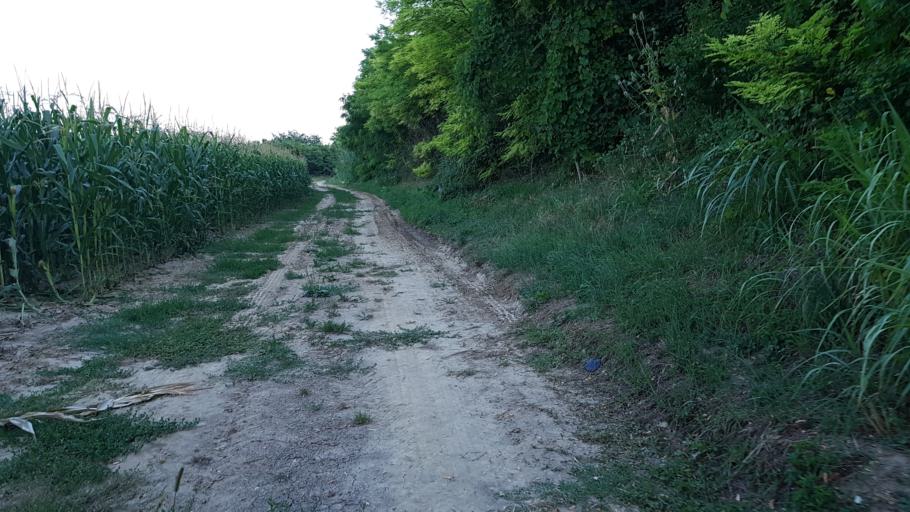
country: IT
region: Friuli Venezia Giulia
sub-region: Provincia di Gorizia
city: San Pier d'Isonzo
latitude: 45.8398
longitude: 13.4595
